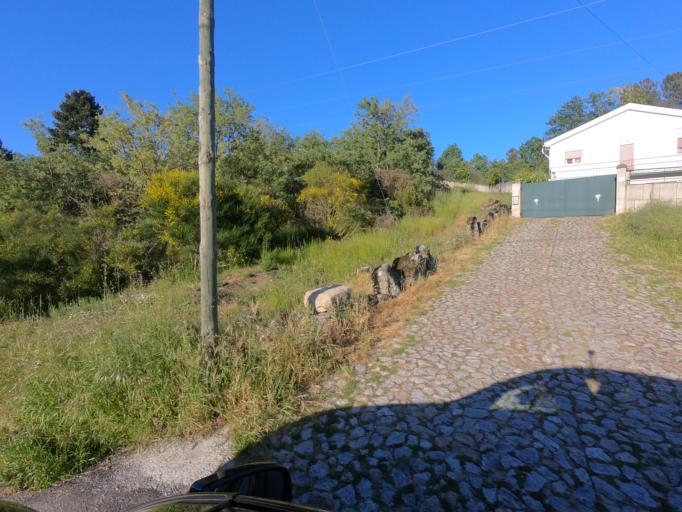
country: PT
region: Vila Real
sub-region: Vila Real
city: Vila Real
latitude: 41.3485
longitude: -7.7263
